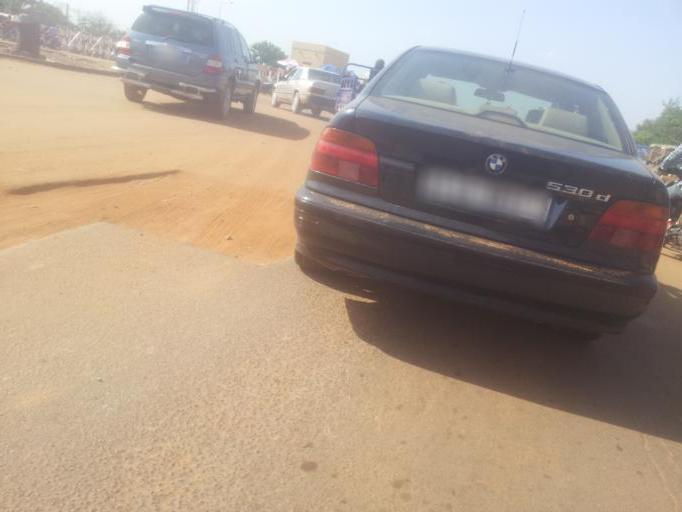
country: BF
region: Centre
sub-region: Kadiogo Province
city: Ouagadougou
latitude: 12.3750
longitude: -1.5695
